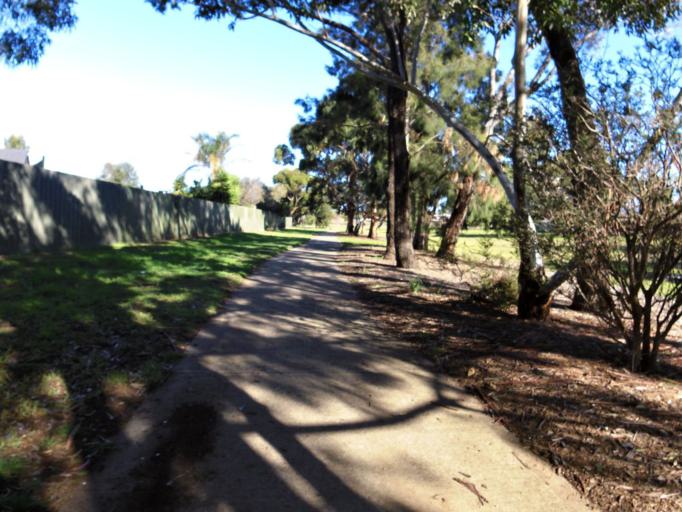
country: AU
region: Victoria
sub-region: Wyndham
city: Tarneit
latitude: -37.8724
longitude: 144.6748
